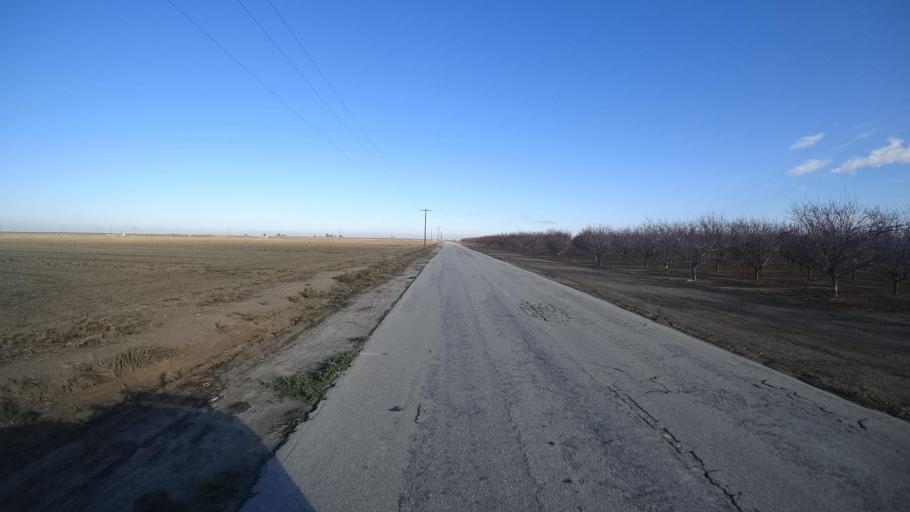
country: US
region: California
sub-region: Kern County
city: Delano
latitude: 35.7579
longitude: -119.3298
